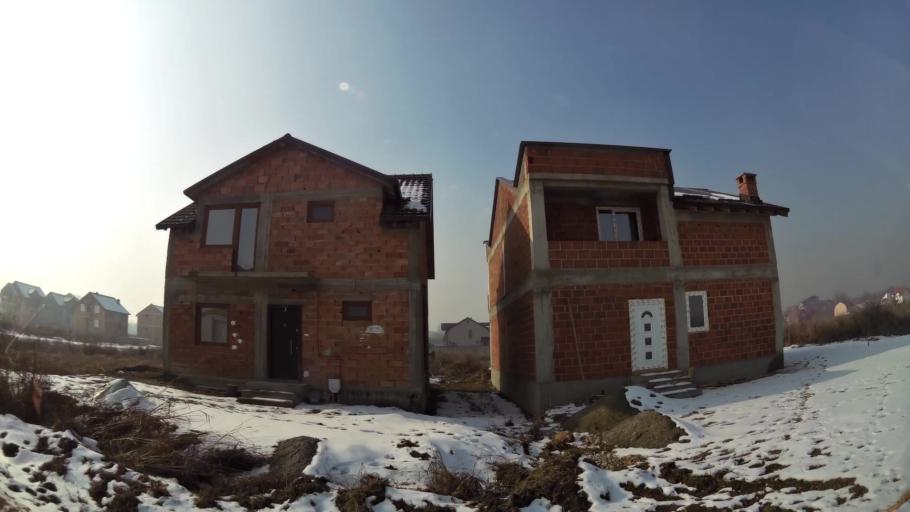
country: MK
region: Kisela Voda
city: Kisela Voda
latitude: 41.9932
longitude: 21.5171
